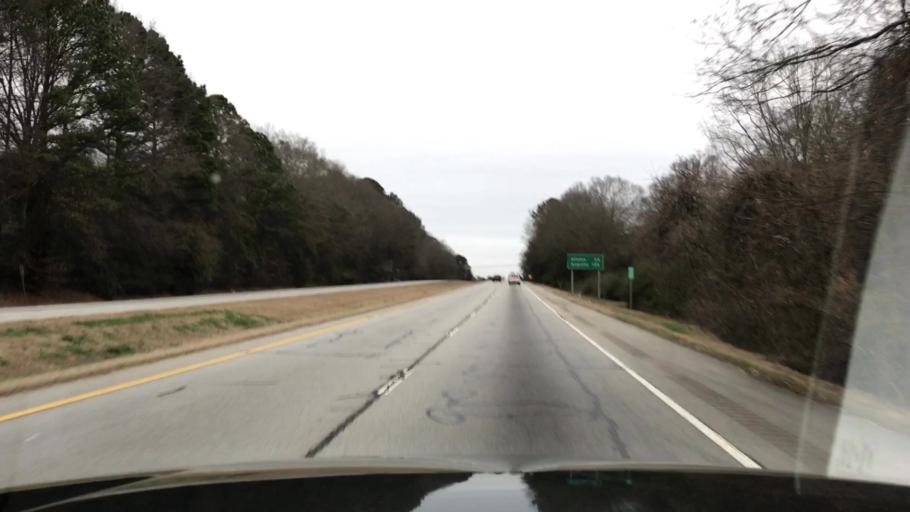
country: US
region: Georgia
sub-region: Walton County
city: Monroe
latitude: 33.8059
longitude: -83.7142
